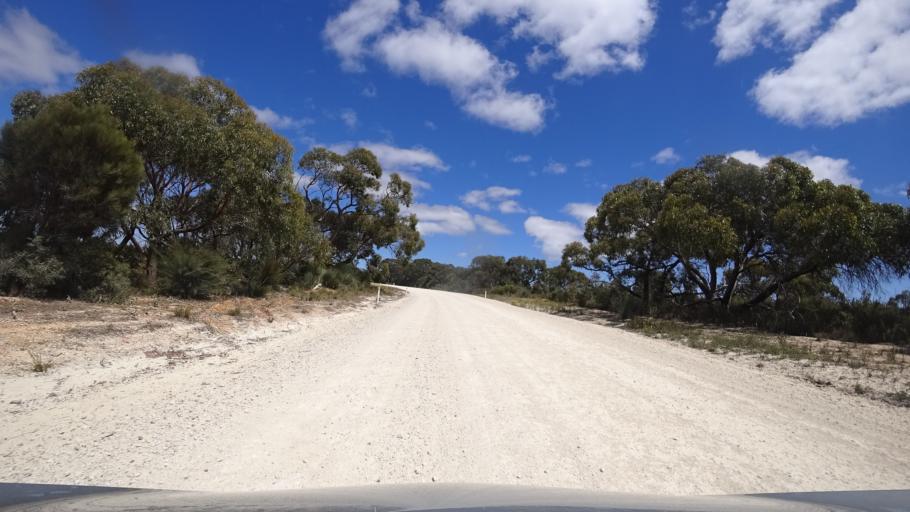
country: AU
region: South Australia
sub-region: Kangaroo Island
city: Kingscote
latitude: -35.6462
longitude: 137.3770
